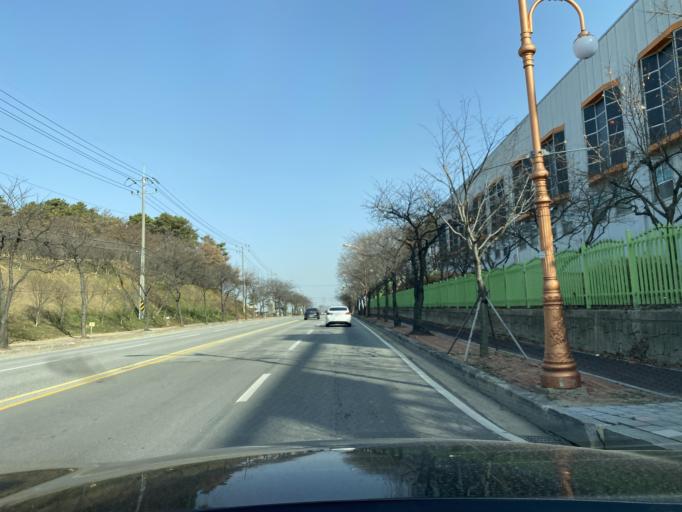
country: KR
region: Chungcheongnam-do
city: Yesan
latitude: 36.7154
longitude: 126.8430
